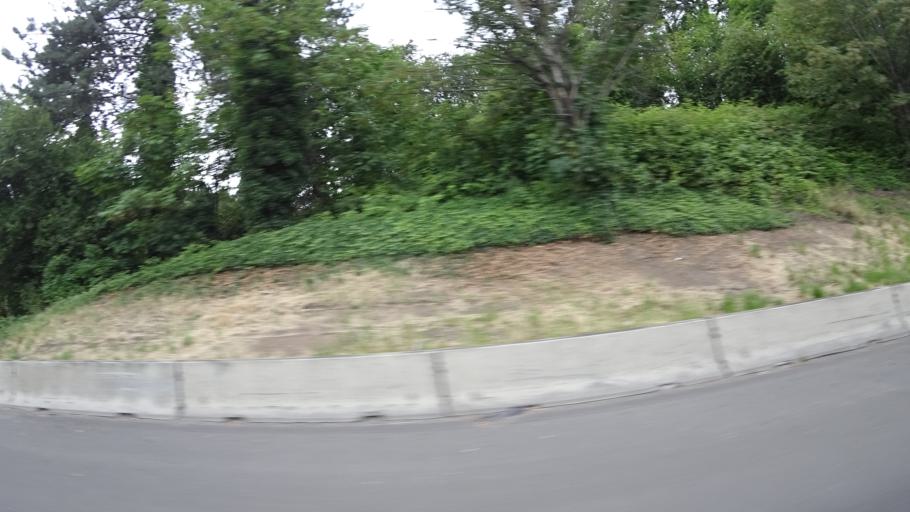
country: US
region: Oregon
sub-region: Multnomah County
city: Portland
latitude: 45.4872
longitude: -122.6791
